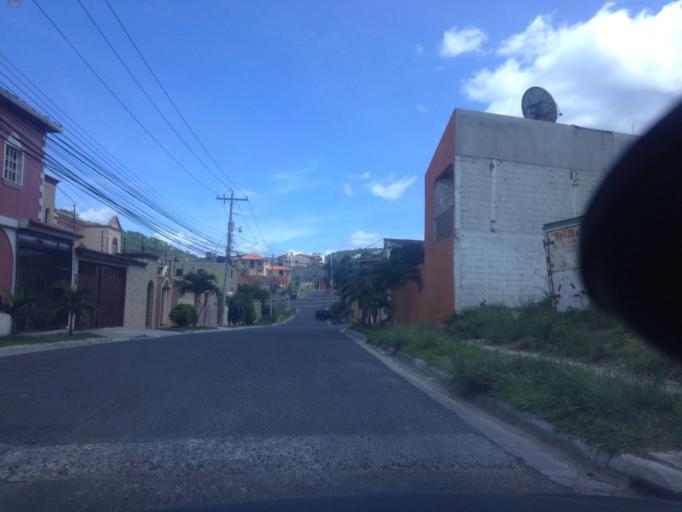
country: HN
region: Francisco Morazan
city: Yaguacire
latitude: 14.0424
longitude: -87.2318
